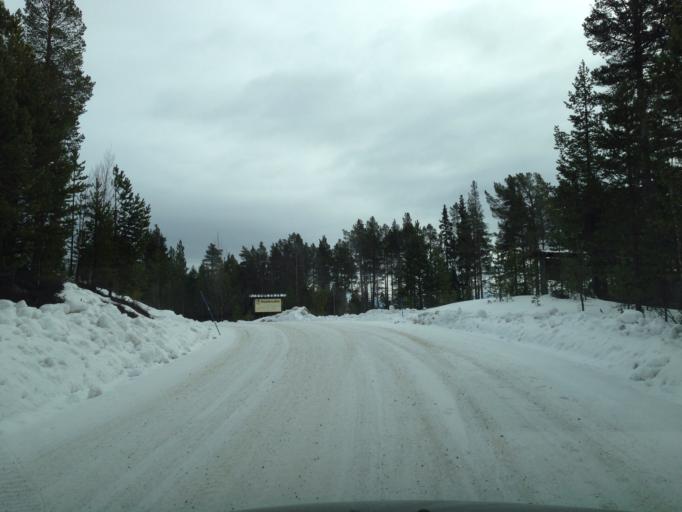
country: SE
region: Jaemtland
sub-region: Harjedalens Kommun
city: Sveg
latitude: 62.1113
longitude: 13.2908
